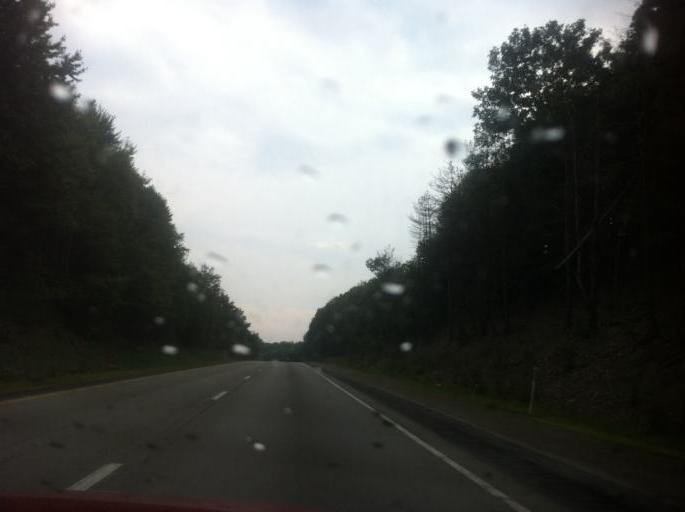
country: US
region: Pennsylvania
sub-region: Clarion County
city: Clarion
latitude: 41.1766
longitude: -79.2530
